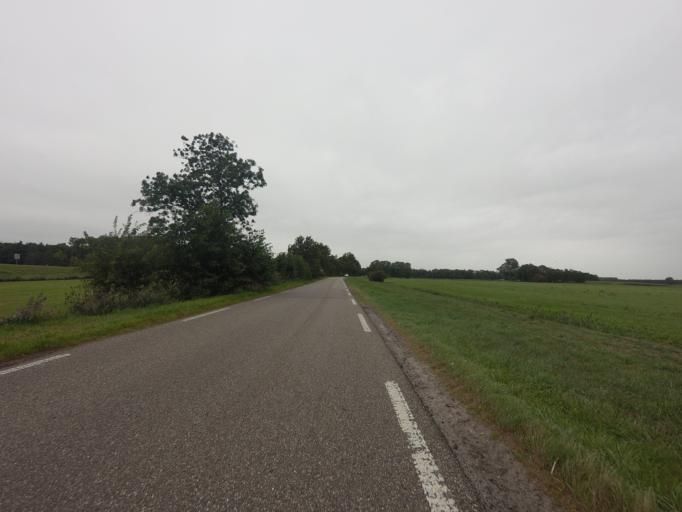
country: NL
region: Friesland
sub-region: Gemeente Opsterland
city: Tijnje
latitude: 53.0235
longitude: 6.0059
